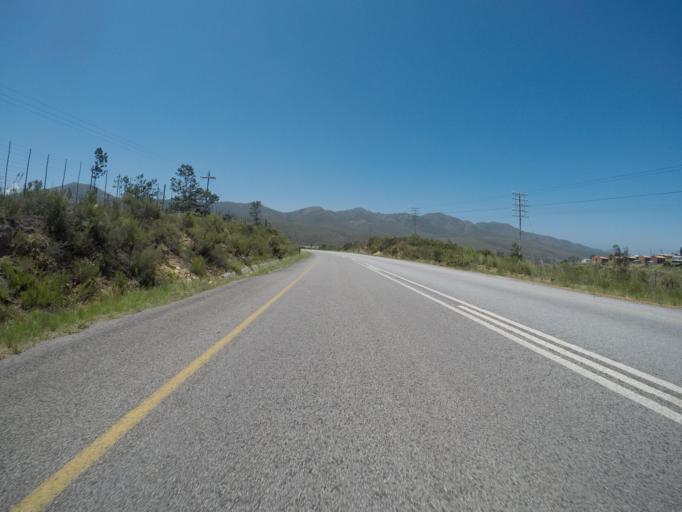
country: ZA
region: Eastern Cape
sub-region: Cacadu District Municipality
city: Kareedouw
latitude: -33.9492
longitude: 24.3027
